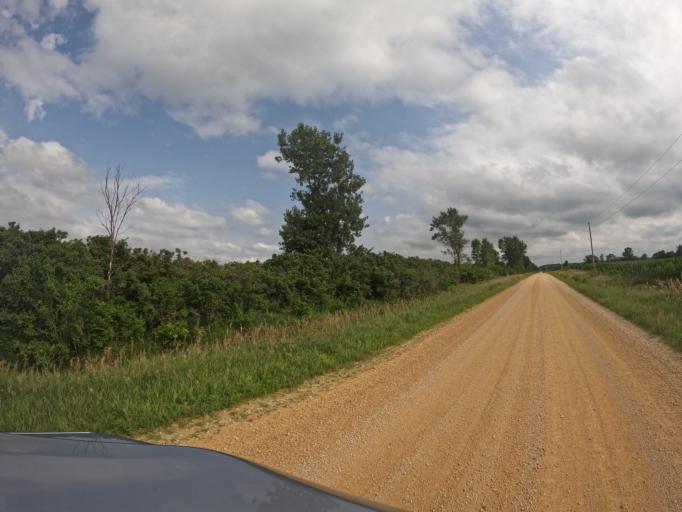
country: US
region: Iowa
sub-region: Clinton County
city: De Witt
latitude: 41.7784
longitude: -90.5684
